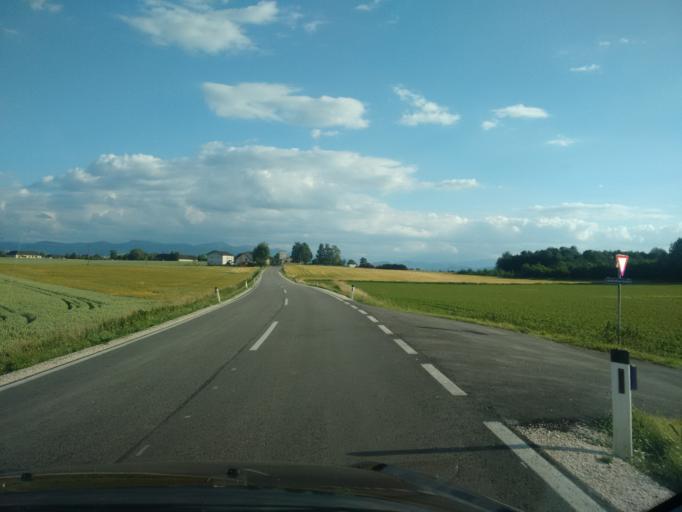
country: AT
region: Upper Austria
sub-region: Politischer Bezirk Steyr-Land
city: Sierning
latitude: 48.0627
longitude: 14.3166
